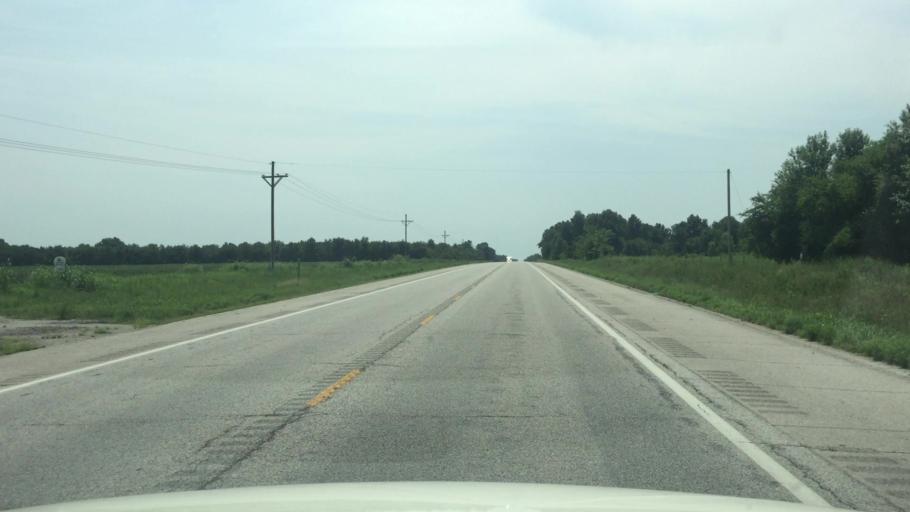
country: US
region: Kansas
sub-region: Cherokee County
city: Galena
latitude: 37.1574
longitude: -94.7043
